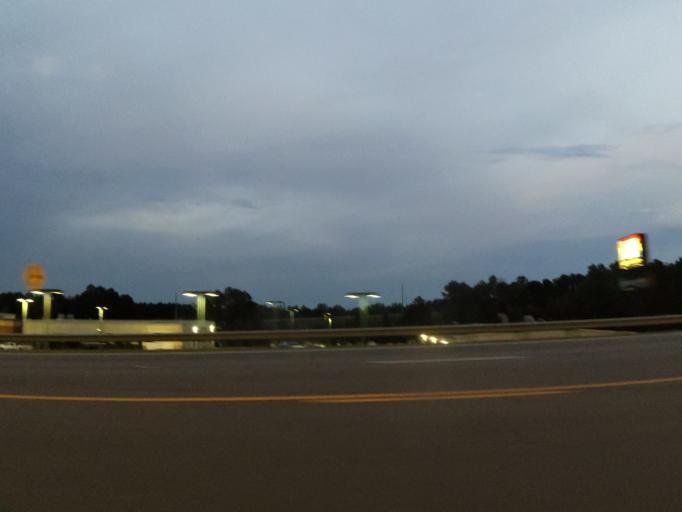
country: US
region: Georgia
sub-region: McDuffie County
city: Thomson
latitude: 33.5141
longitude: -82.5025
